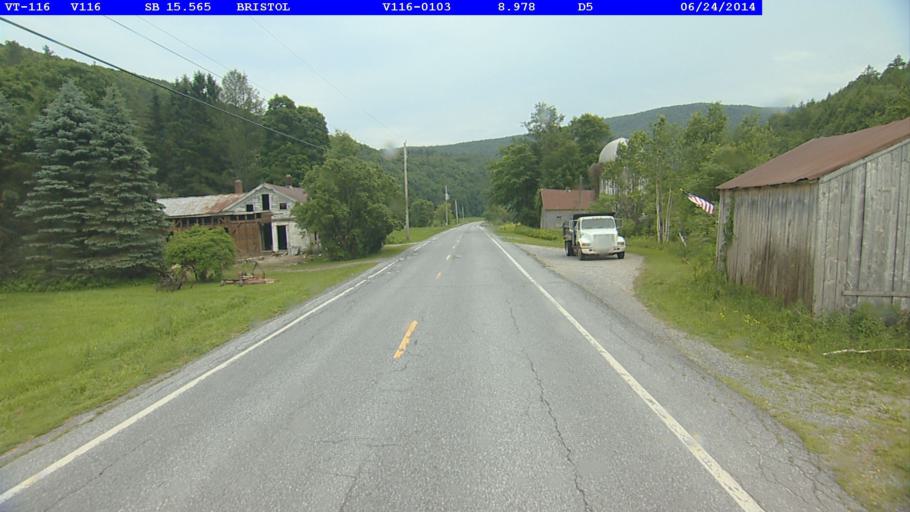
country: US
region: Vermont
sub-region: Addison County
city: Bristol
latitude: 44.1400
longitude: -73.0454
